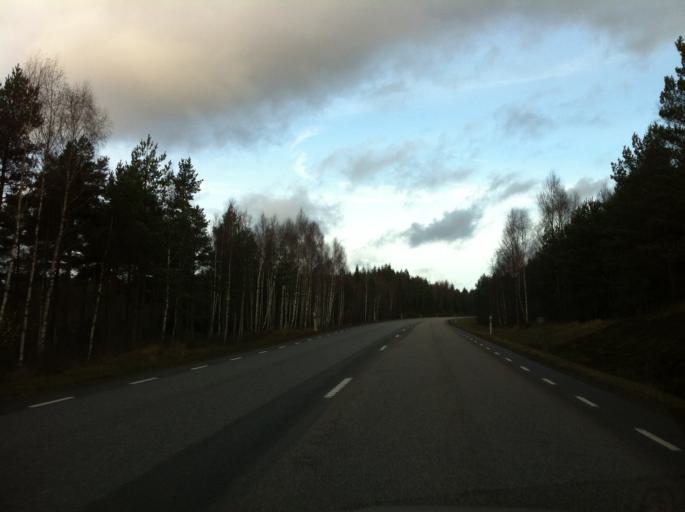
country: SE
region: Kronoberg
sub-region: Almhults Kommun
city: AElmhult
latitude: 56.5547
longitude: 14.1735
